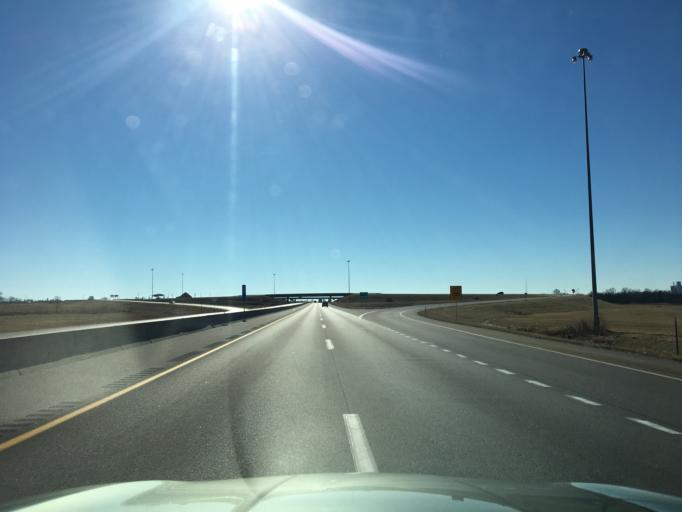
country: US
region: Kansas
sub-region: Sumner County
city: Wellington
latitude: 37.2829
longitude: -97.3403
